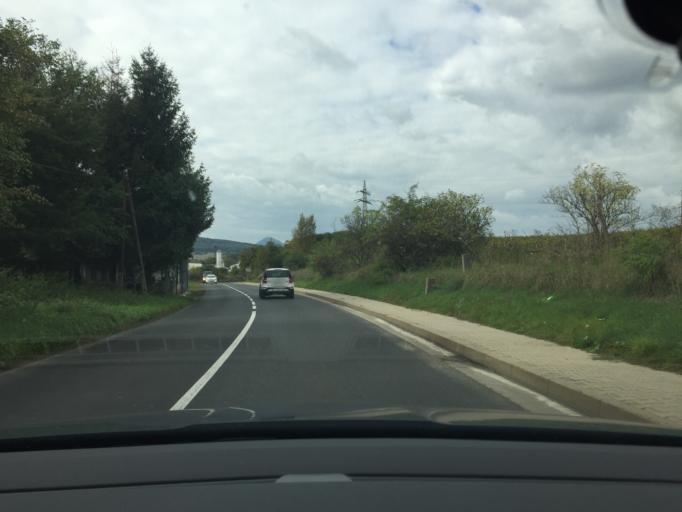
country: CZ
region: Ustecky
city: Lovosice
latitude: 50.5295
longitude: 14.0755
